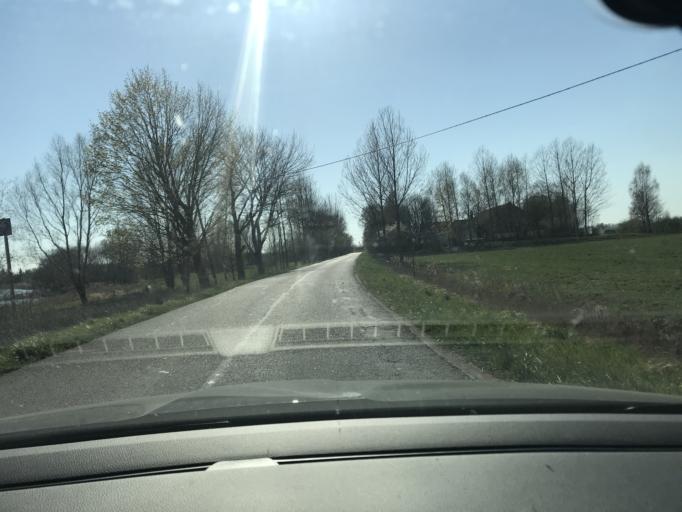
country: PL
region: Pomeranian Voivodeship
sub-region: Powiat nowodworski
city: Sztutowo
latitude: 54.2991
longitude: 19.1461
